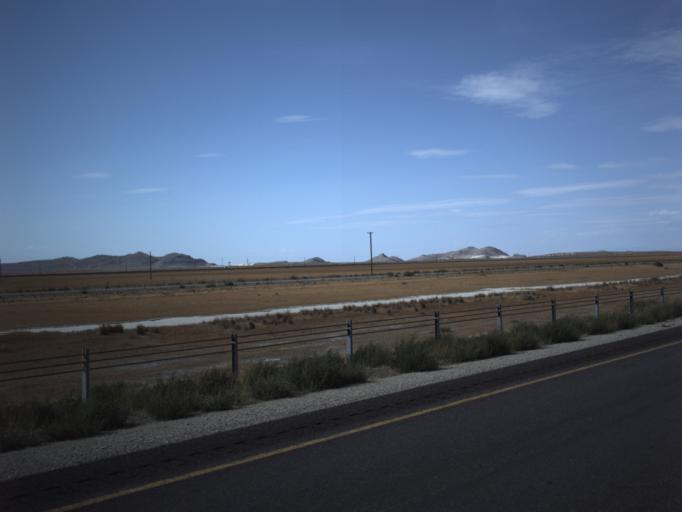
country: US
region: Utah
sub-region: Tooele County
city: Grantsville
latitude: 40.7271
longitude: -113.2325
